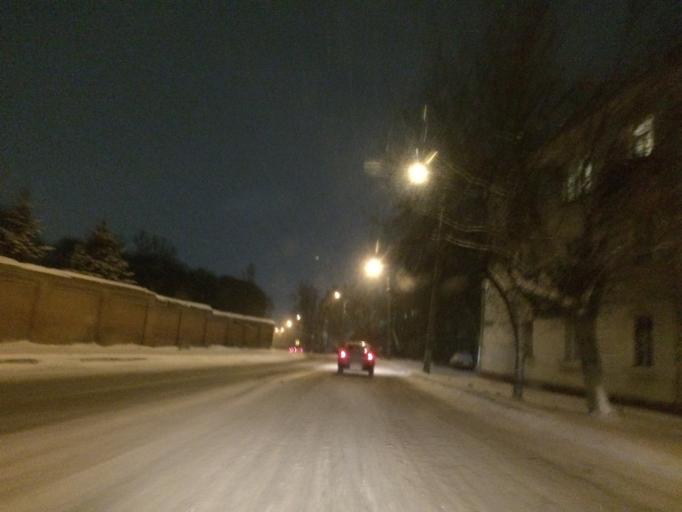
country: RU
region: Tula
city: Tula
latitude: 54.1761
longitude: 37.6129
